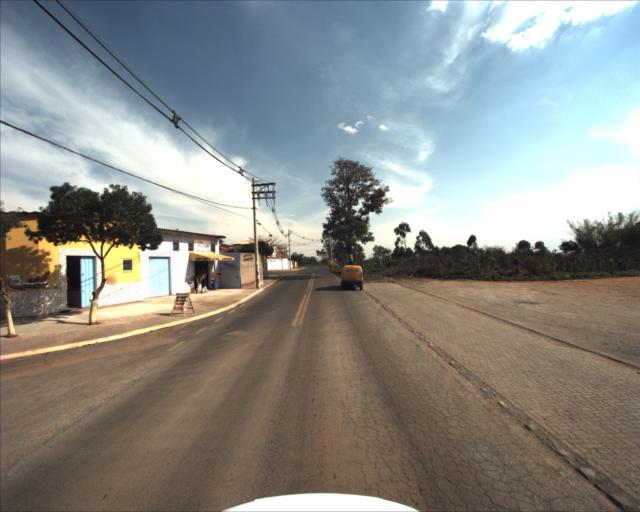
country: BR
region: Sao Paulo
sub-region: Sorocaba
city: Sorocaba
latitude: -23.4945
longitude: -47.5321
